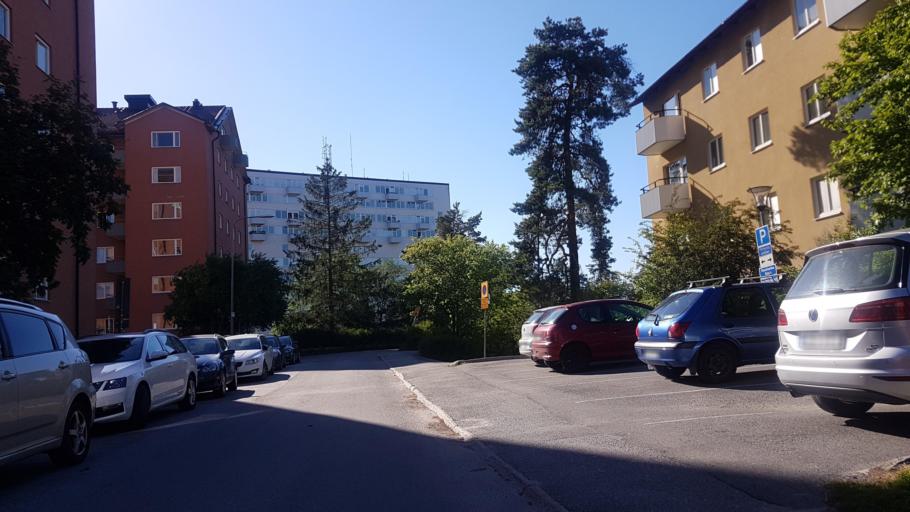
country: SE
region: Stockholm
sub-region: Nacka Kommun
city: Nacka
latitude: 59.2905
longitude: 18.1198
